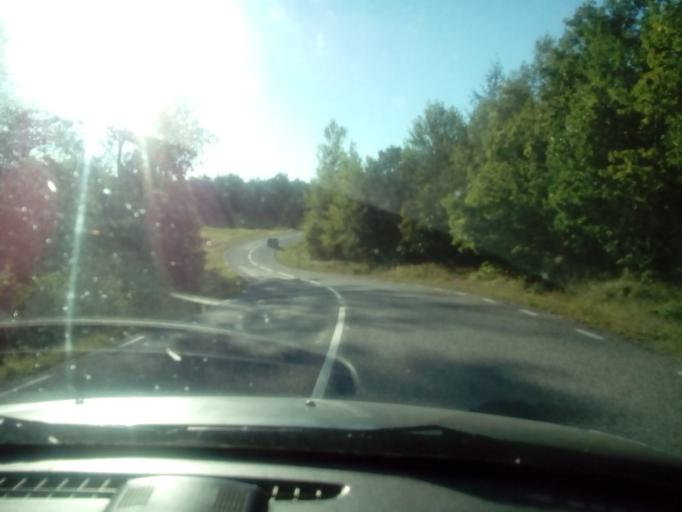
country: SE
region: Kalmar
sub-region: Vasterviks Kommun
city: Gamleby
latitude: 57.7932
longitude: 16.3774
